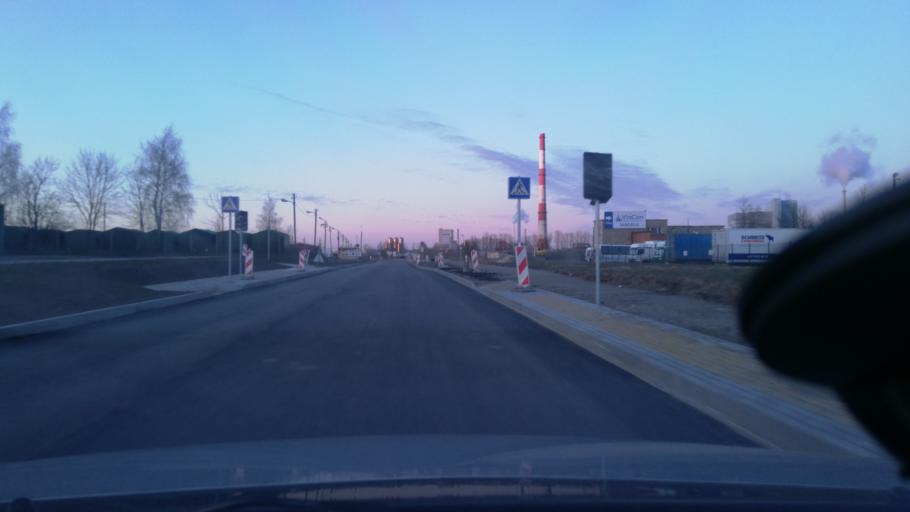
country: LT
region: Klaipedos apskritis
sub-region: Klaipeda
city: Klaipeda
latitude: 55.6785
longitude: 21.1912
